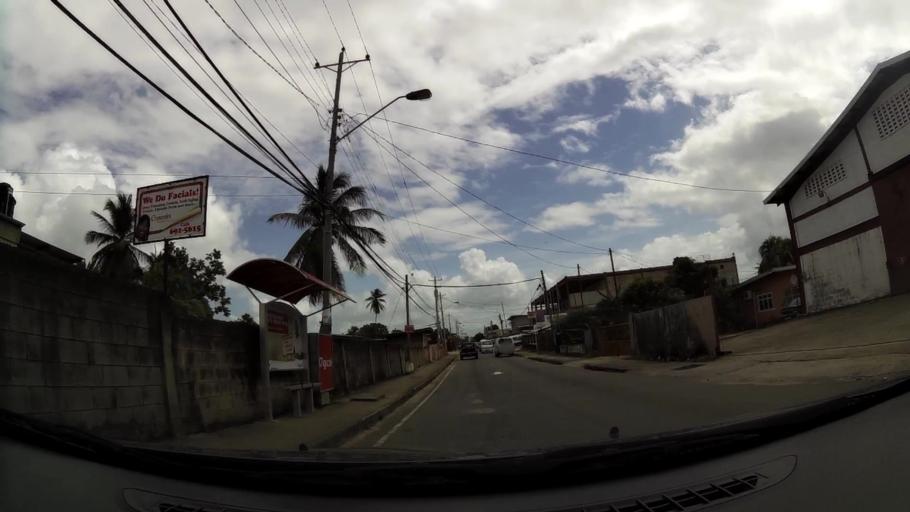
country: TT
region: Tunapuna/Piarco
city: Arouca
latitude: 10.6341
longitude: -61.3277
